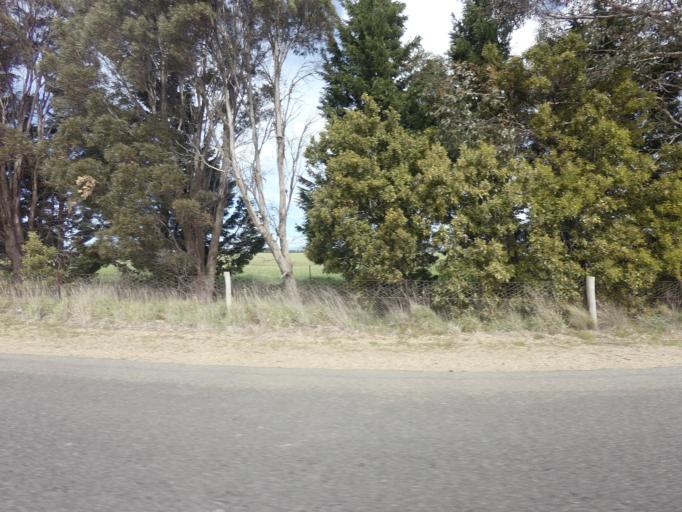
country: AU
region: Tasmania
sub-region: Northern Midlands
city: Longford
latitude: -41.6610
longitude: 147.1715
